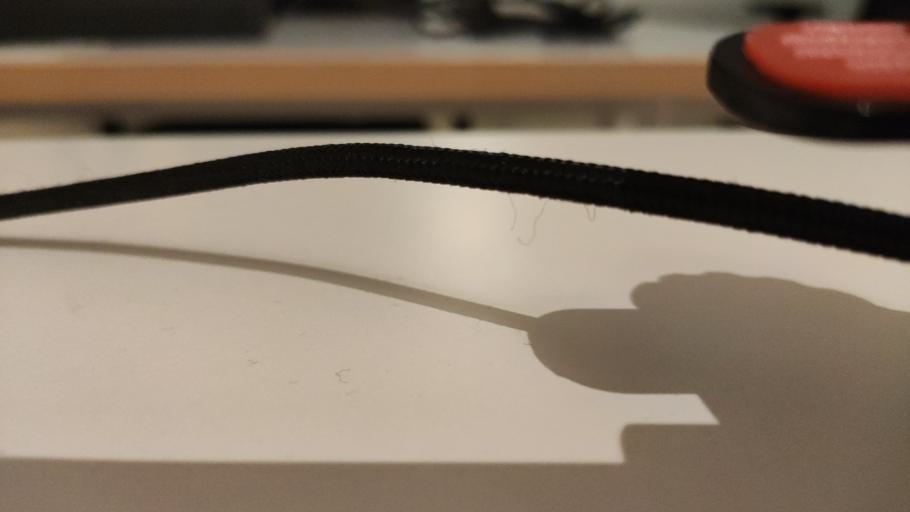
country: RU
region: Moskovskaya
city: Rybnoye
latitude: 56.4133
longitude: 37.6681
